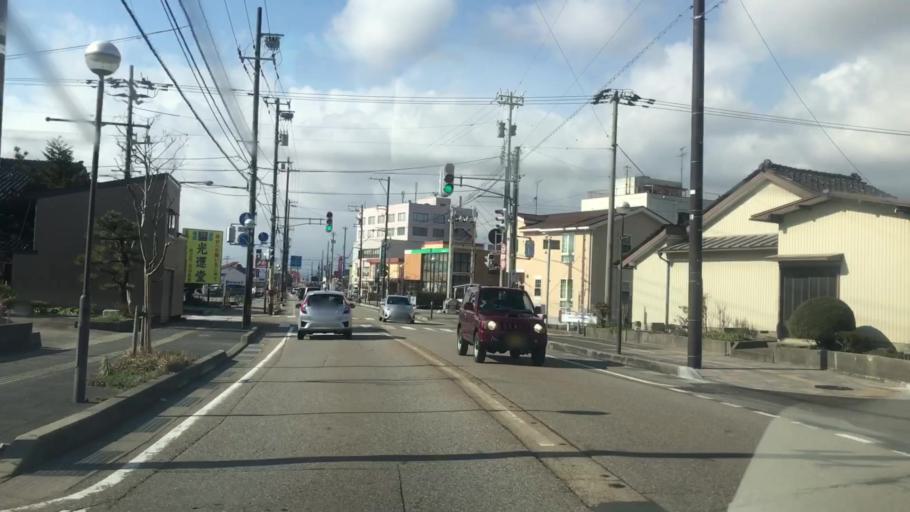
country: JP
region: Toyama
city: Takaoka
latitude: 36.7325
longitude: 137.0520
